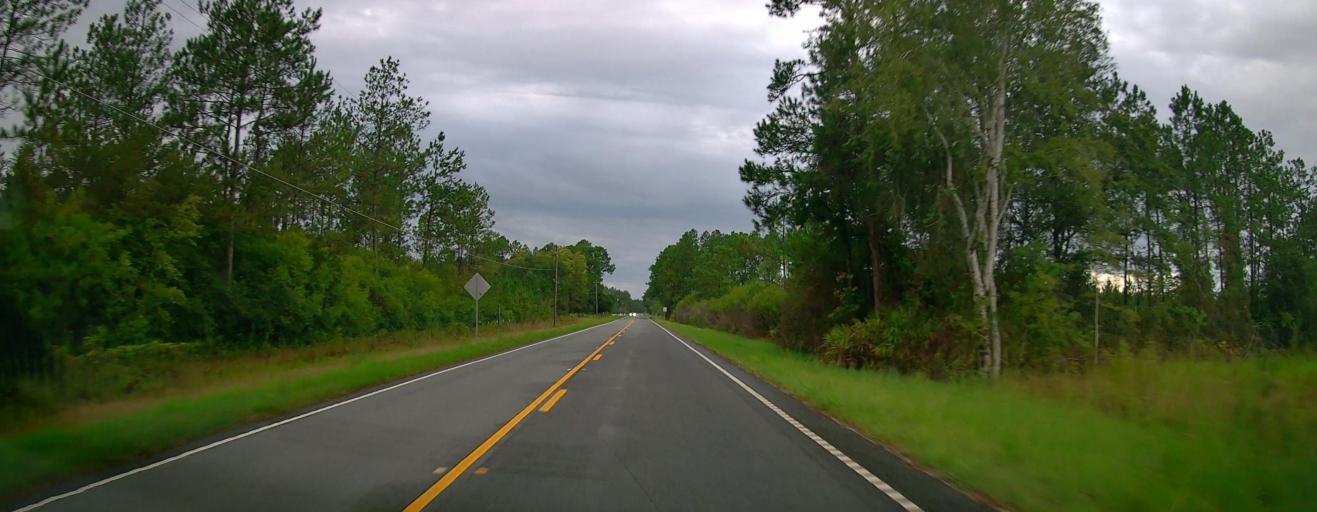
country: US
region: Georgia
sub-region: Ware County
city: Deenwood
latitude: 31.2803
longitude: -82.4264
